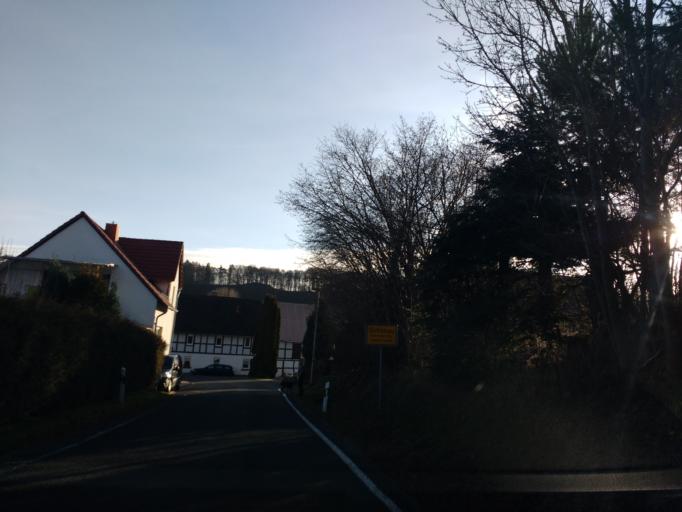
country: DE
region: Thuringia
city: Burgwalde
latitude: 51.3743
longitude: 10.0417
